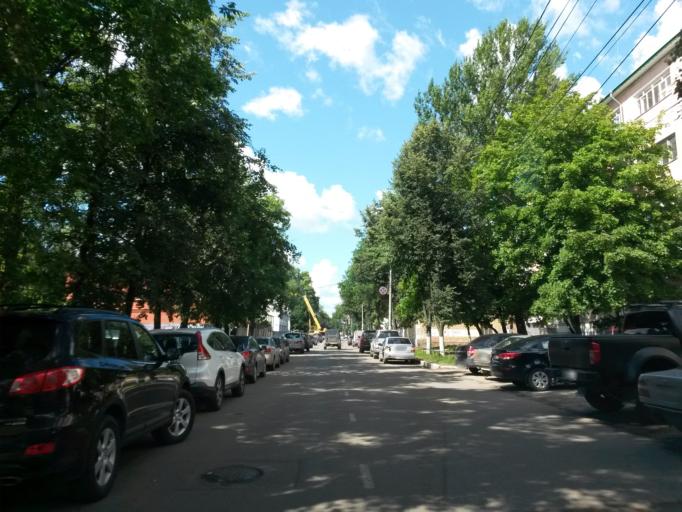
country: RU
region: Jaroslavl
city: Yaroslavl
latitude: 57.6302
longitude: 39.8734
